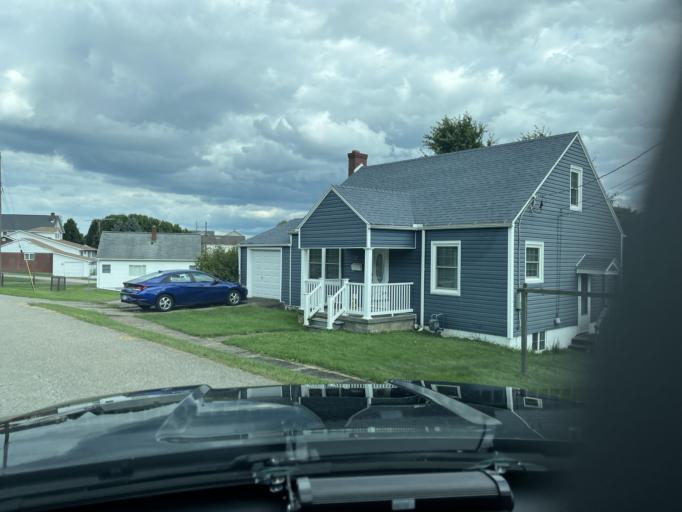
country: US
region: Pennsylvania
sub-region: Fayette County
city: South Uniontown
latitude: 39.8933
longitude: -79.7475
